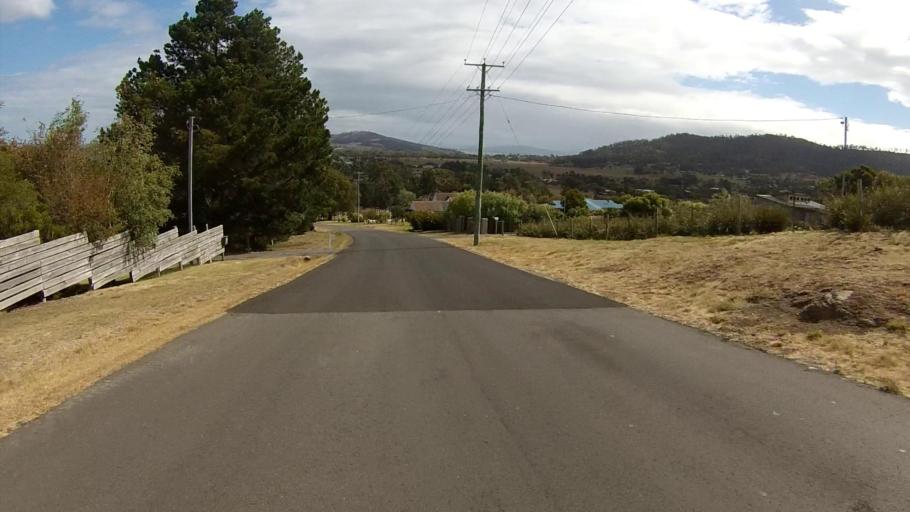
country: AU
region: Tasmania
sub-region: Clarence
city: Acton Park
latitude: -42.8853
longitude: 147.5012
